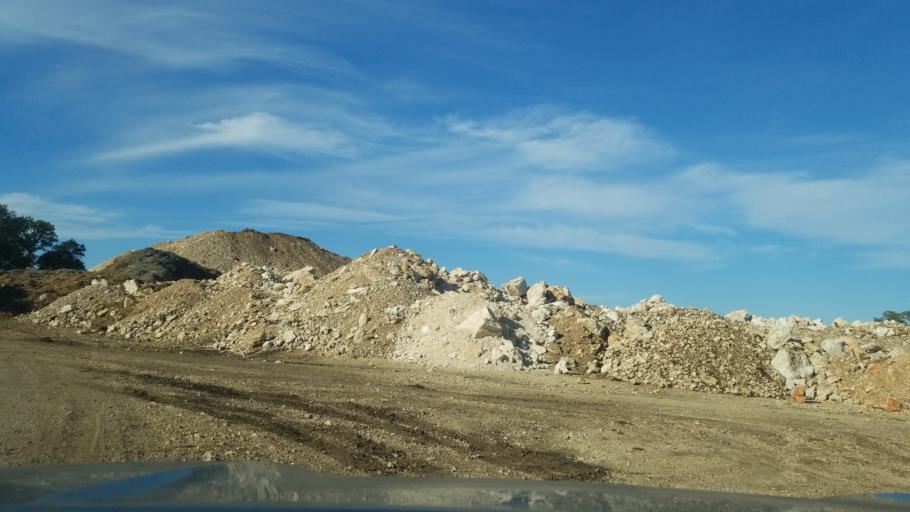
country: US
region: Texas
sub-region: Comal County
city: Canyon Lake
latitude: 29.7829
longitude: -98.2884
